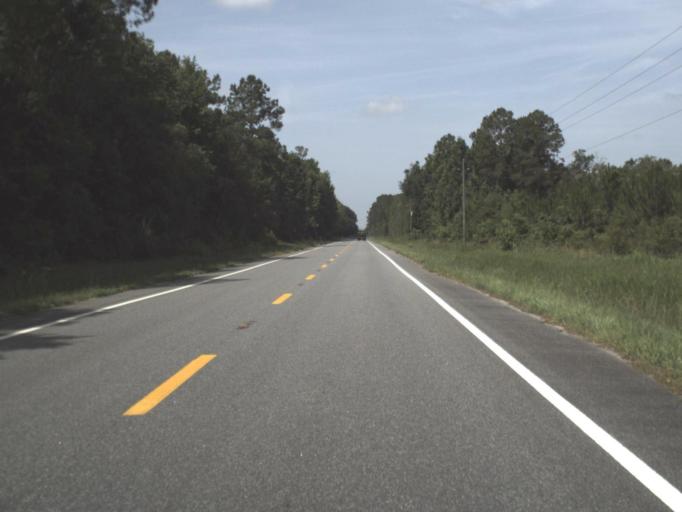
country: US
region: Florida
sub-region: Lafayette County
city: Mayo
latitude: 29.9392
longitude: -83.2684
